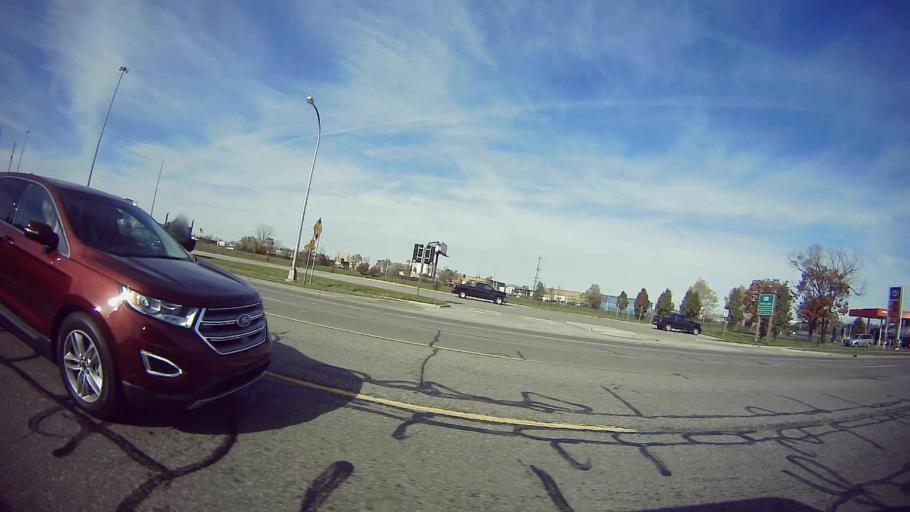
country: US
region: Michigan
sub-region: Wayne County
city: Dearborn
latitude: 42.3274
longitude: -83.1577
